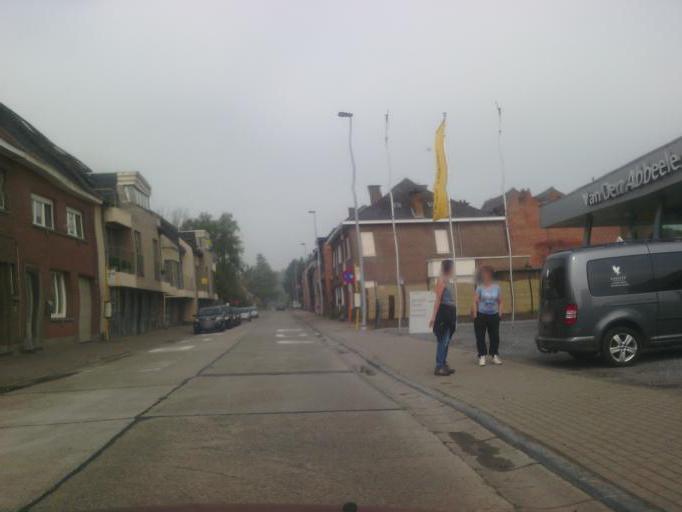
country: BE
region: Flanders
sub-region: Provincie Oost-Vlaanderen
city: Aalst
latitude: 50.9873
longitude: 4.0455
